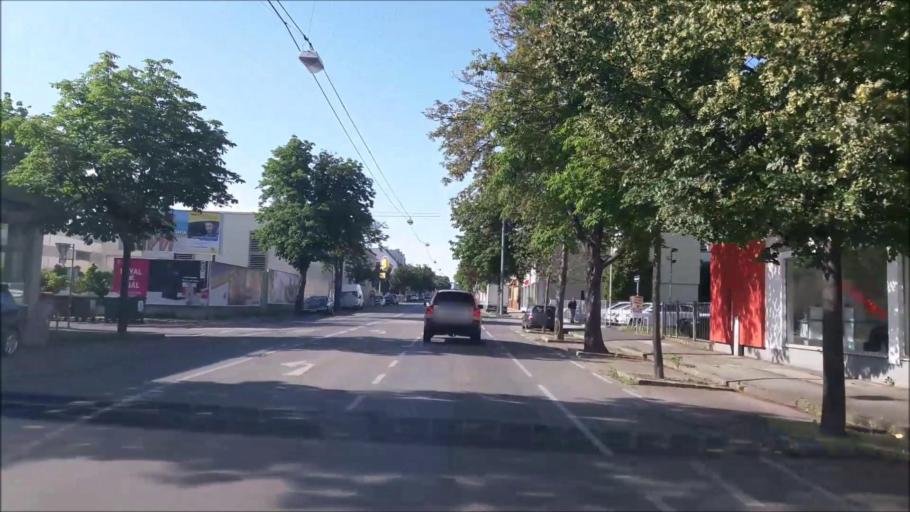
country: AT
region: Lower Austria
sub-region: Politischer Bezirk Wien-Umgebung
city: Leopoldsdorf
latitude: 48.1404
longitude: 16.3829
